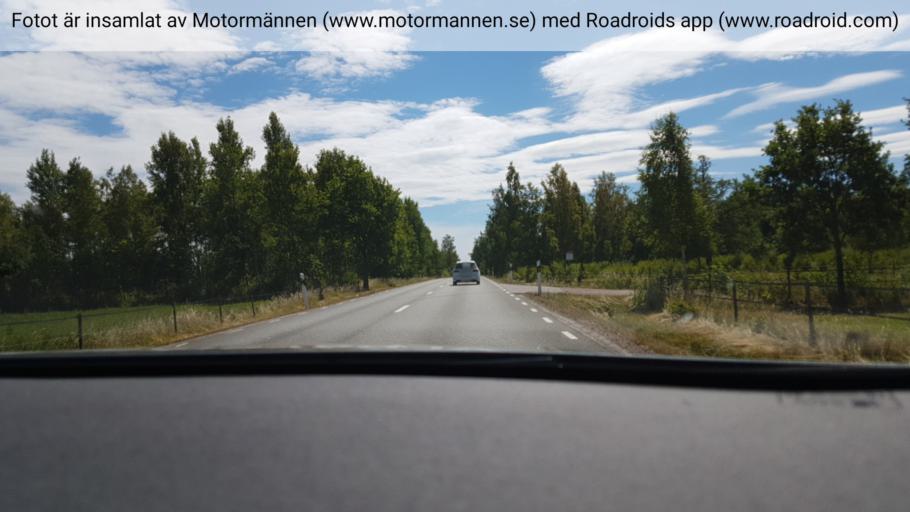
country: SE
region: Joenkoeping
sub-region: Jonkopings Kommun
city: Asa
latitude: 57.9911
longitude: 14.7527
